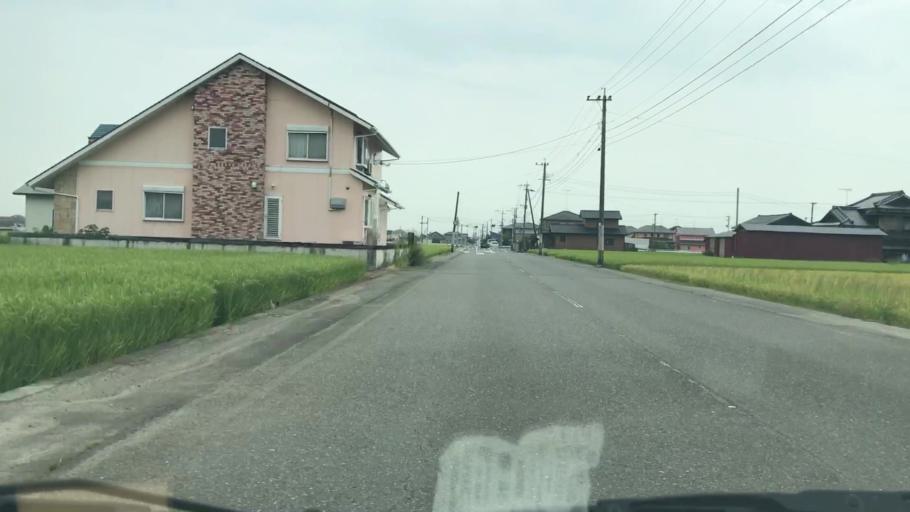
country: JP
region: Saga Prefecture
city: Saga-shi
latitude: 33.2222
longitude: 130.1775
